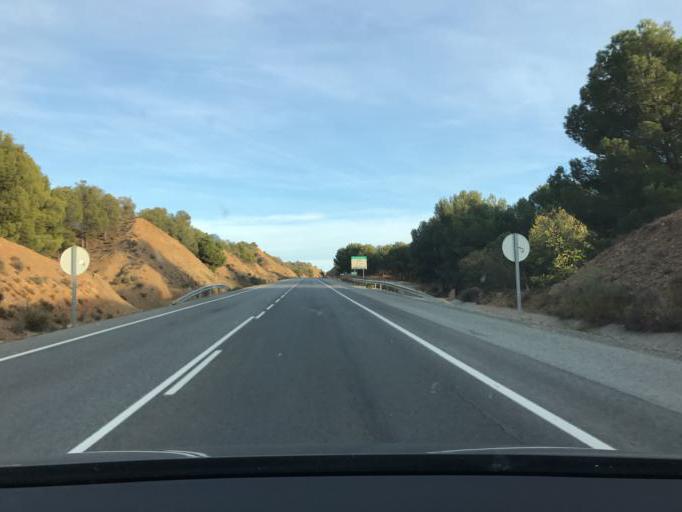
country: ES
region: Andalusia
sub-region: Provincia de Granada
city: Guadix
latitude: 37.2715
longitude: -3.1036
